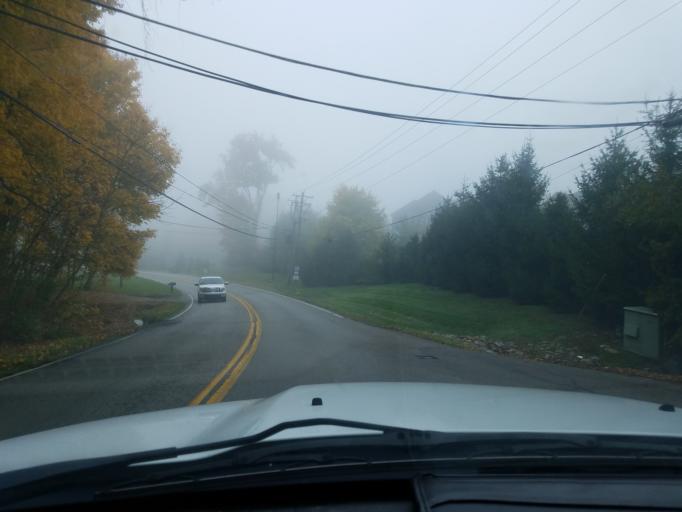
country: US
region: Indiana
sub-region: Floyd County
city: New Albany
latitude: 38.3250
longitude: -85.8602
